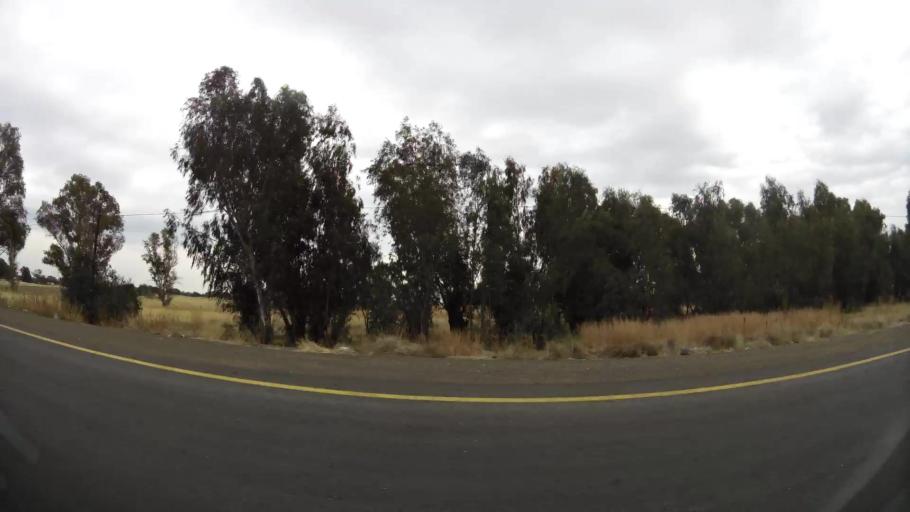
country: ZA
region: Orange Free State
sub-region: Fezile Dabi District Municipality
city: Kroonstad
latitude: -27.6181
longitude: 27.2343
